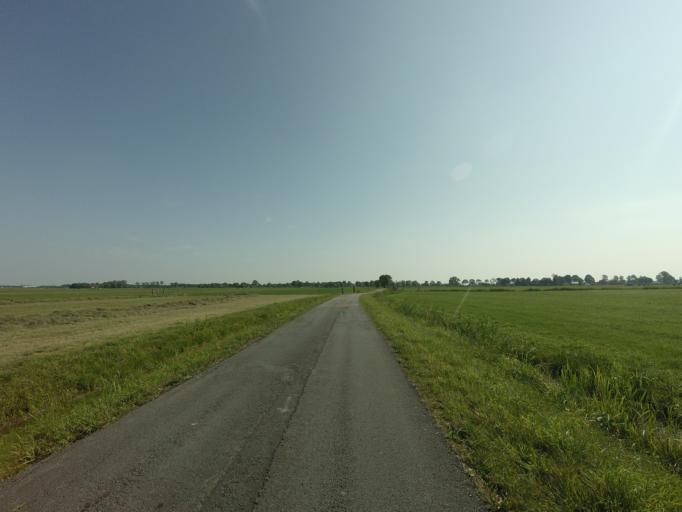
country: NL
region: Groningen
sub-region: Gemeente Zuidhorn
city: Zuidhorn
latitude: 53.2161
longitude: 6.4316
